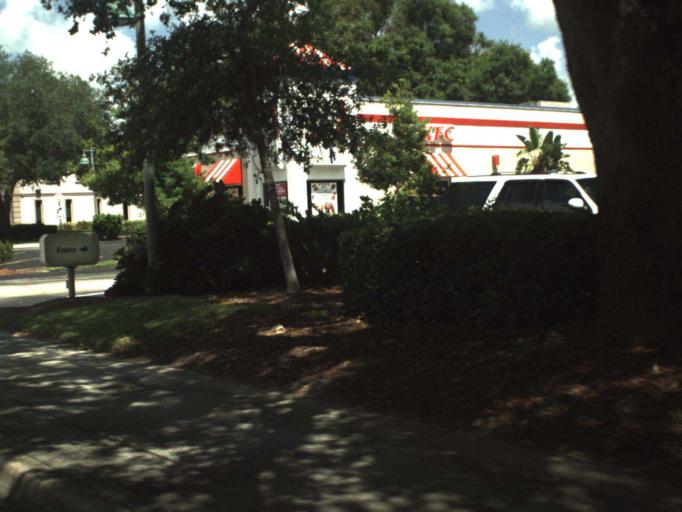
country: US
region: Florida
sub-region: Indian River County
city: Vero Beach South
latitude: 27.6386
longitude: -80.4272
